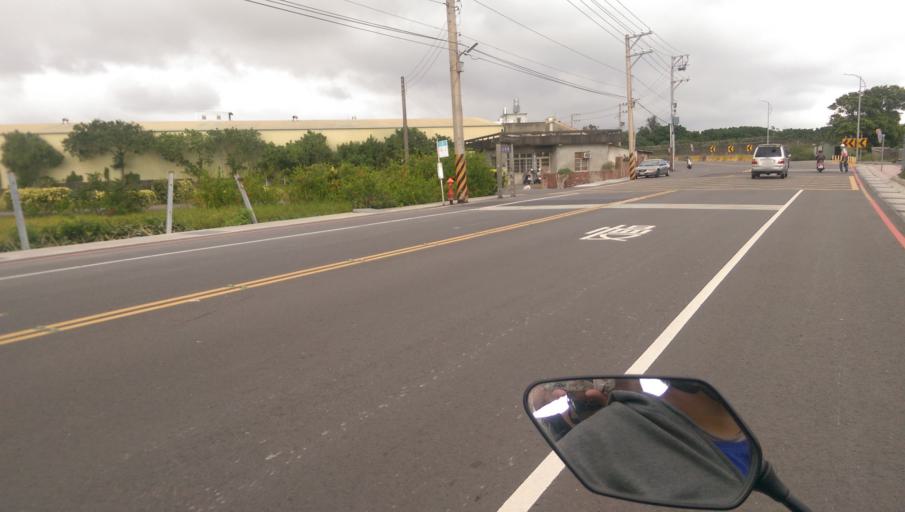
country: TW
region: Taiwan
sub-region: Hsinchu
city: Hsinchu
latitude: 24.8134
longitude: 120.9282
